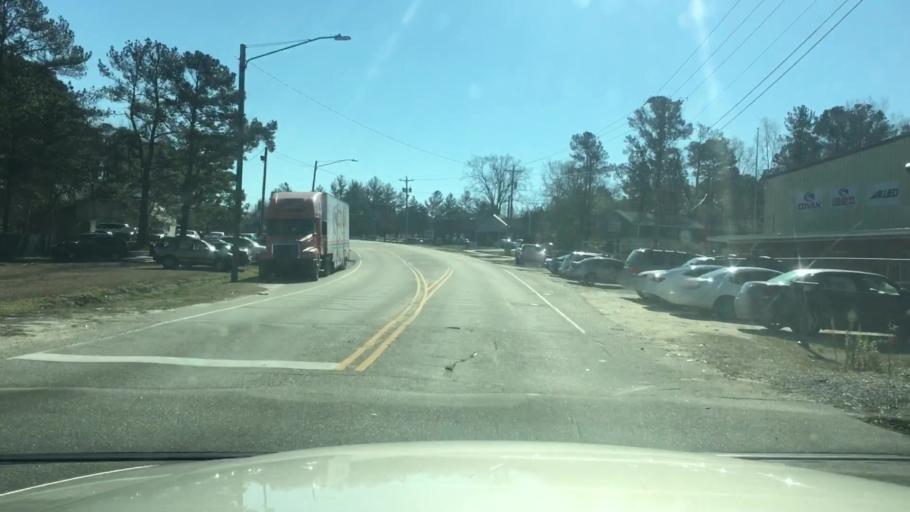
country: US
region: North Carolina
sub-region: Cumberland County
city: Fayetteville
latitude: 35.0380
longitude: -78.8961
